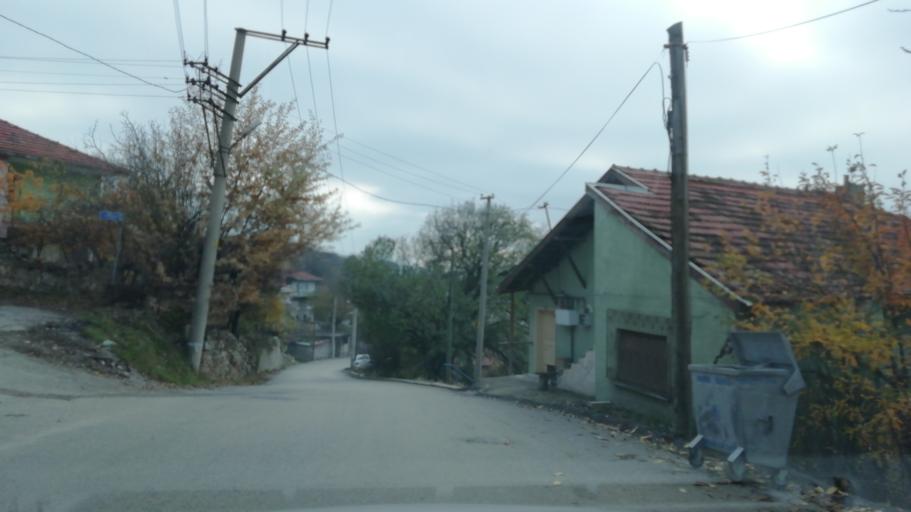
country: TR
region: Karabuk
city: Karabuk
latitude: 41.2183
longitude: 32.6278
